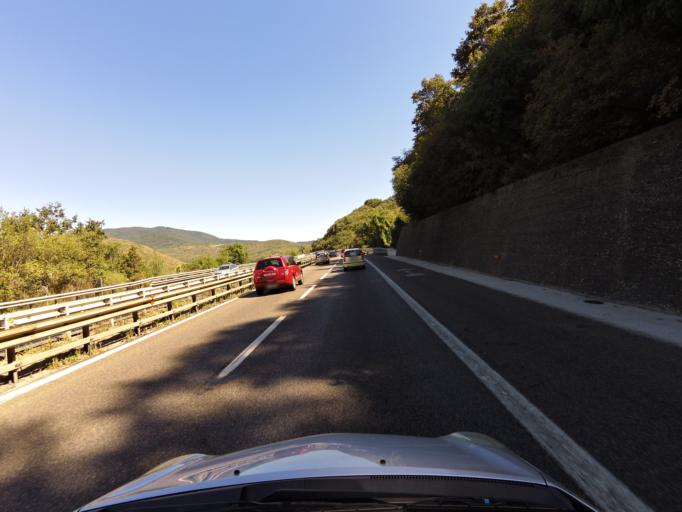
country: IT
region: Tuscany
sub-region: Province of Florence
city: Carraia
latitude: 43.9030
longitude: 11.1941
